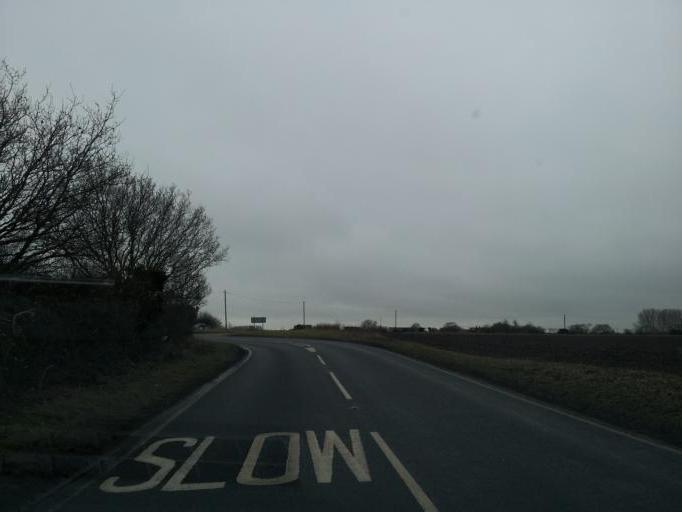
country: GB
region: England
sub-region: Essex
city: Manningtree
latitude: 51.9358
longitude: 1.0626
